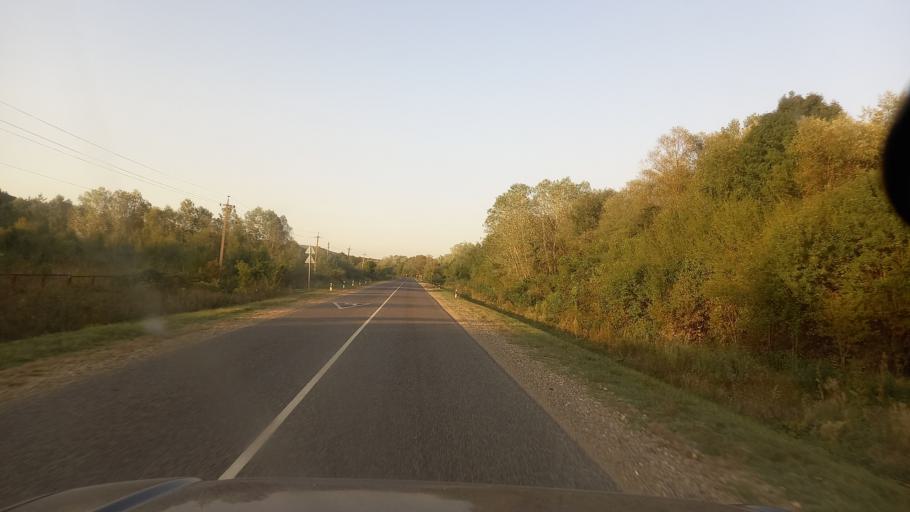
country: RU
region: Krasnodarskiy
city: Smolenskaya
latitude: 44.7547
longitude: 38.7648
